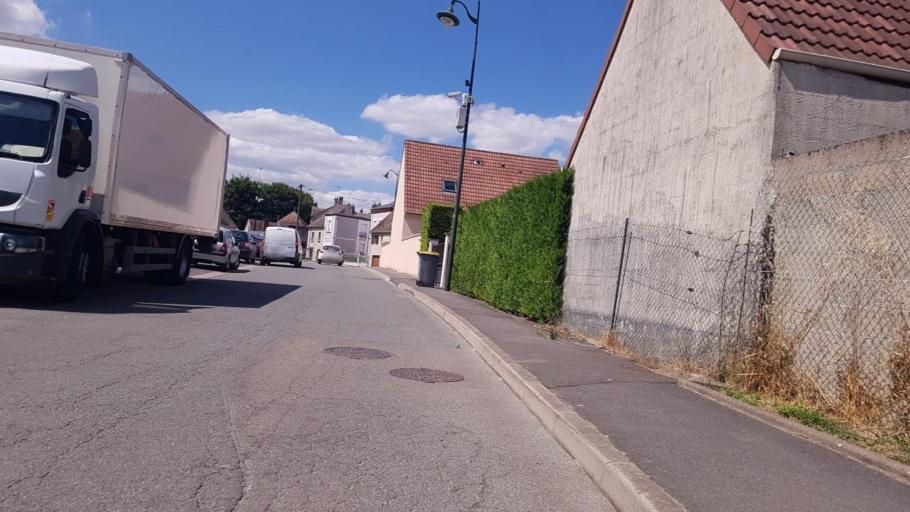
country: FR
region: Ile-de-France
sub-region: Departement de Seine-et-Marne
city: Longperrier
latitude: 49.0094
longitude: 2.6655
